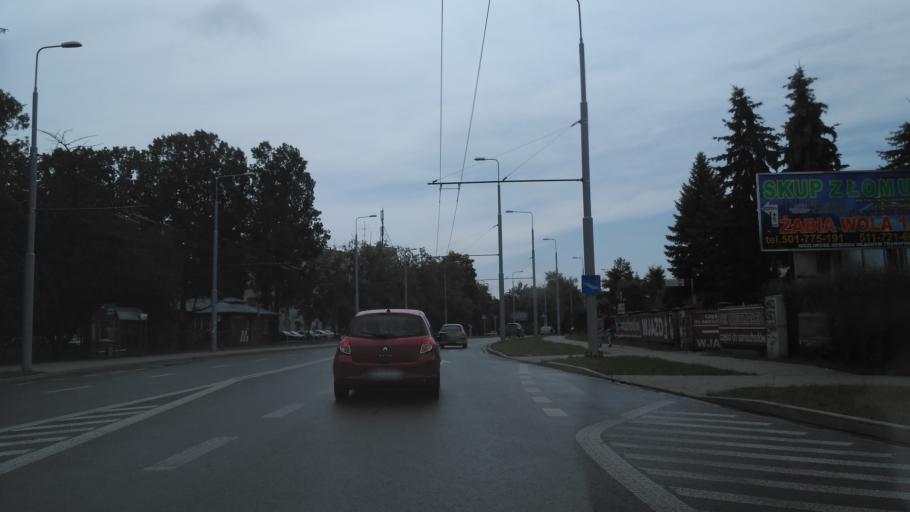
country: PL
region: Lublin Voivodeship
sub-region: Powiat lubelski
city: Lublin
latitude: 51.2062
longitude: 22.5868
